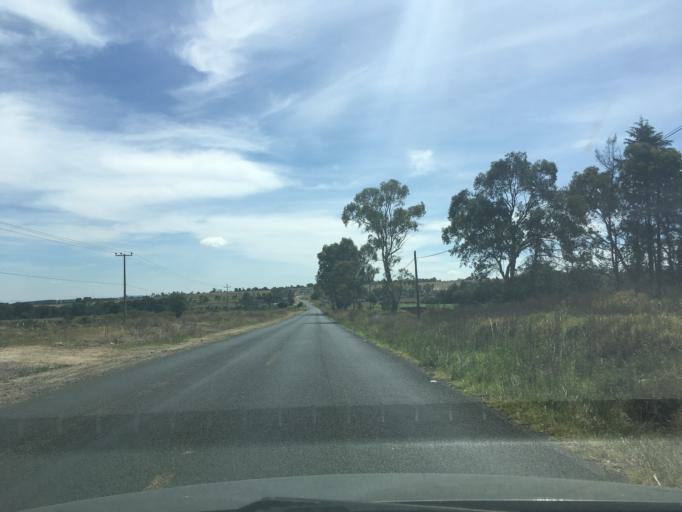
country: MX
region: Queretaro
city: Amealco
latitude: 20.1989
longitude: -100.1356
